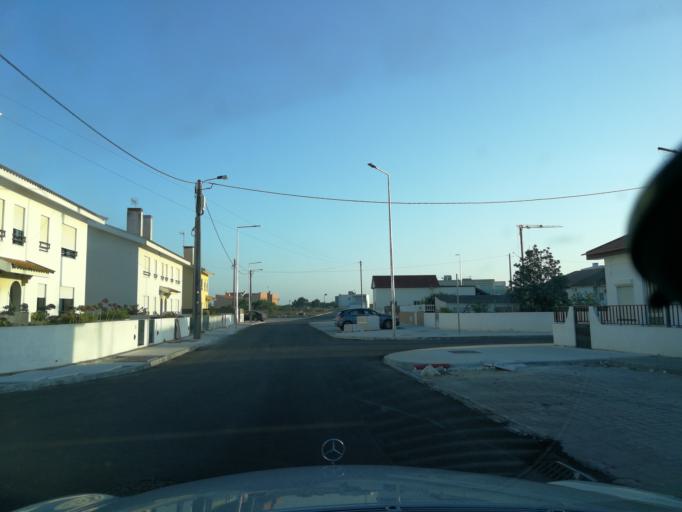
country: PT
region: Aveiro
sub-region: Murtosa
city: Murtosa
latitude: 40.7587
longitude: -8.7099
